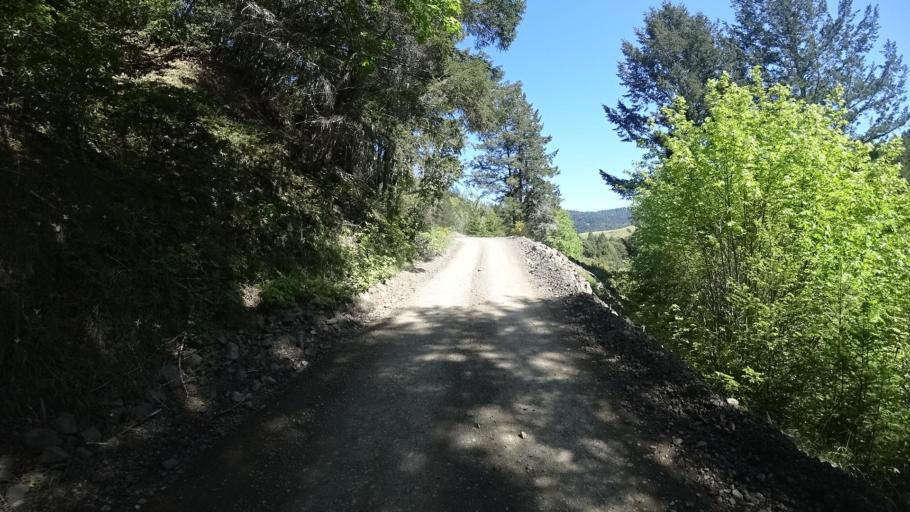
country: US
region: California
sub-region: Humboldt County
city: Rio Dell
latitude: 40.2242
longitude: -124.1114
